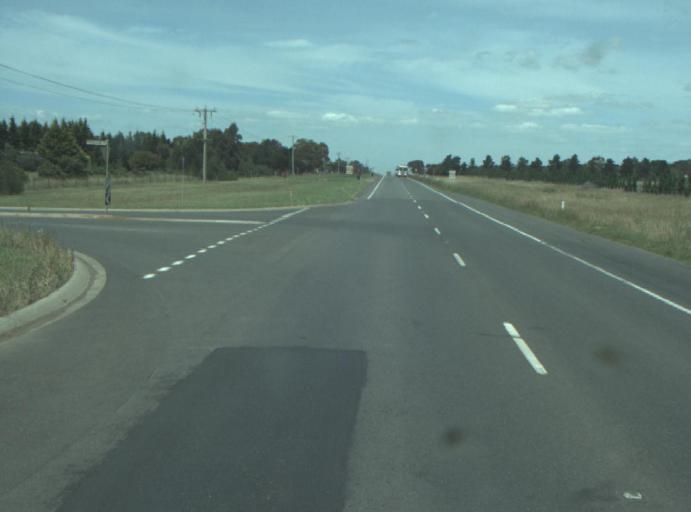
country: AU
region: Victoria
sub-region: Greater Geelong
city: Lara
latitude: -38.0175
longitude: 144.3520
